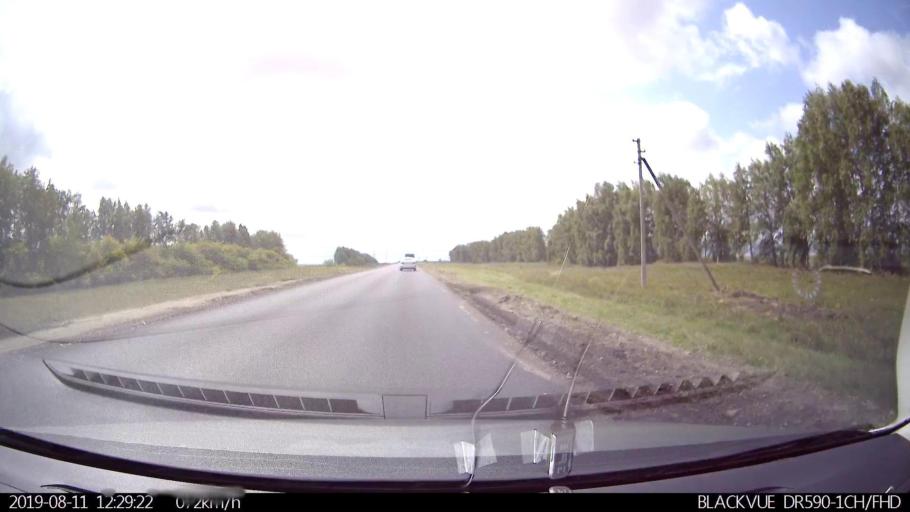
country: RU
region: Ulyanovsk
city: Ignatovka
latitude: 53.8354
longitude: 47.9032
